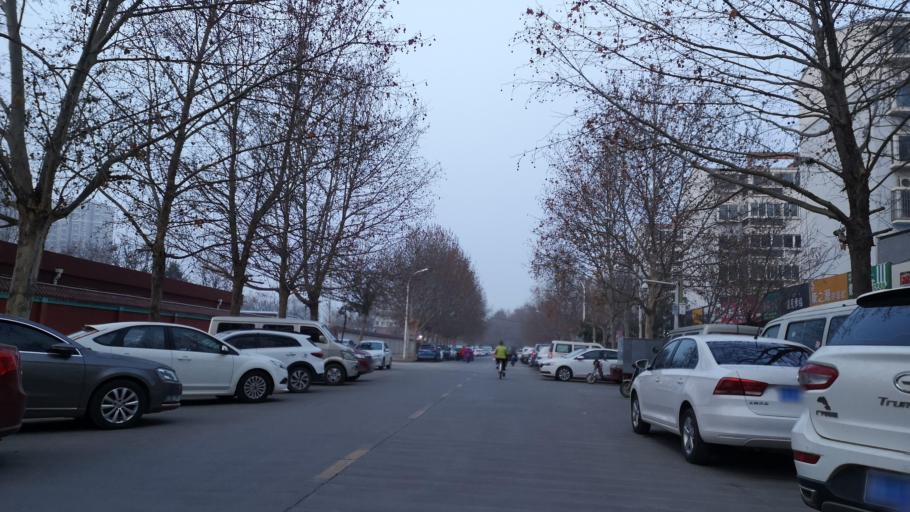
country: CN
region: Henan Sheng
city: Zhongyuanlu
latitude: 35.7554
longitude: 115.0612
